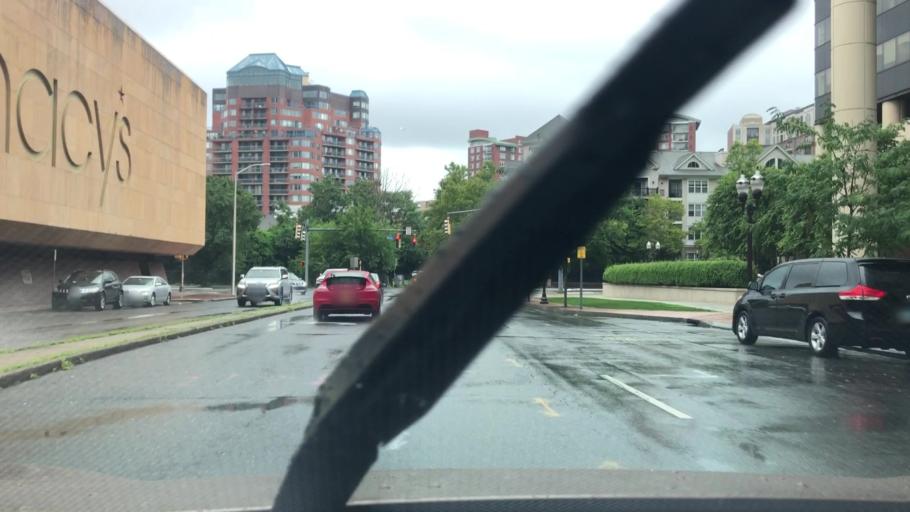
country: US
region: Connecticut
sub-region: Fairfield County
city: Stamford
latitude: 41.0544
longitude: -73.5361
